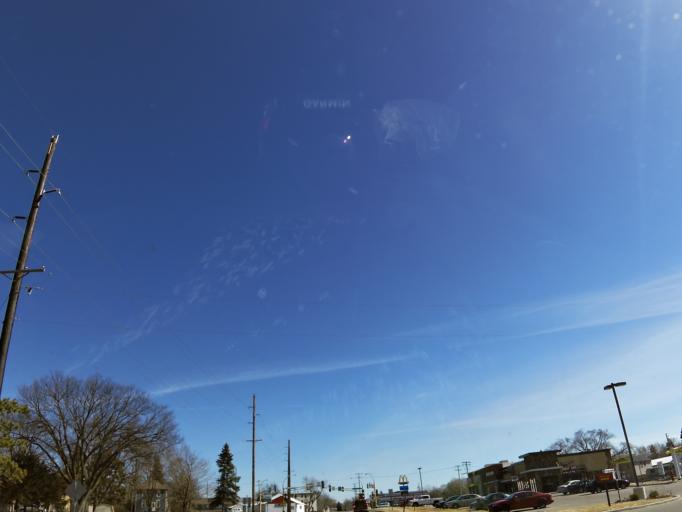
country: US
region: Minnesota
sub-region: Wright County
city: Annandale
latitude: 45.2632
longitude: -94.1290
